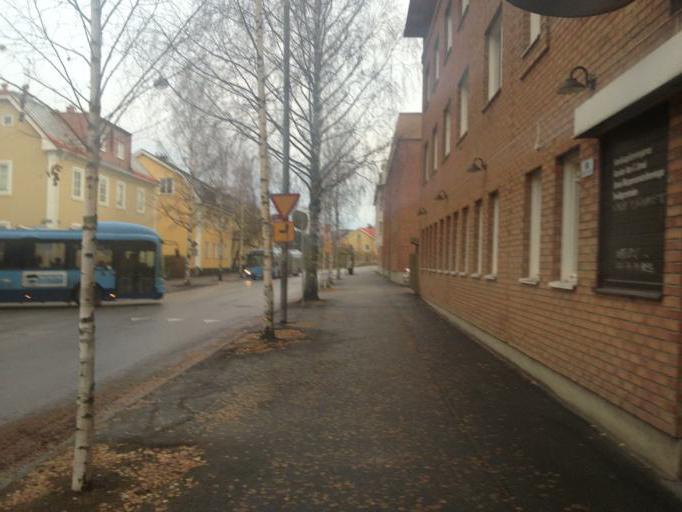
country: SE
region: Vaesterbotten
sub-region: Umea Kommun
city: Umea
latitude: 63.8220
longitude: 20.2802
